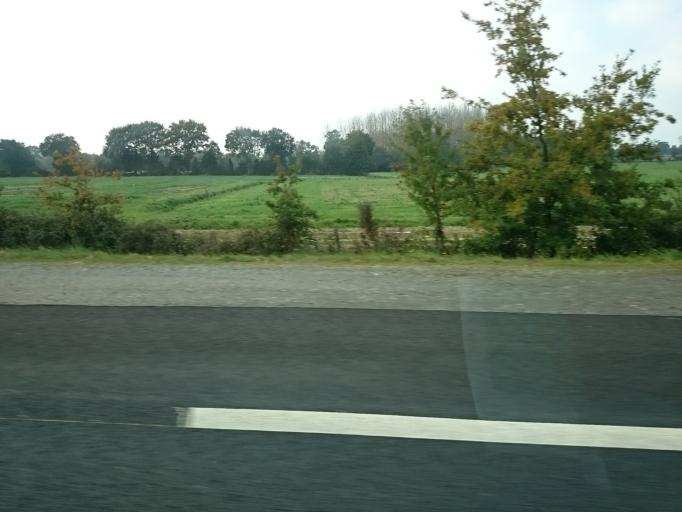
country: FR
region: Brittany
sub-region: Departement d'Ille-et-Vilaine
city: Chatillon-sur-Seiche
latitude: 48.0582
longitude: -1.6801
